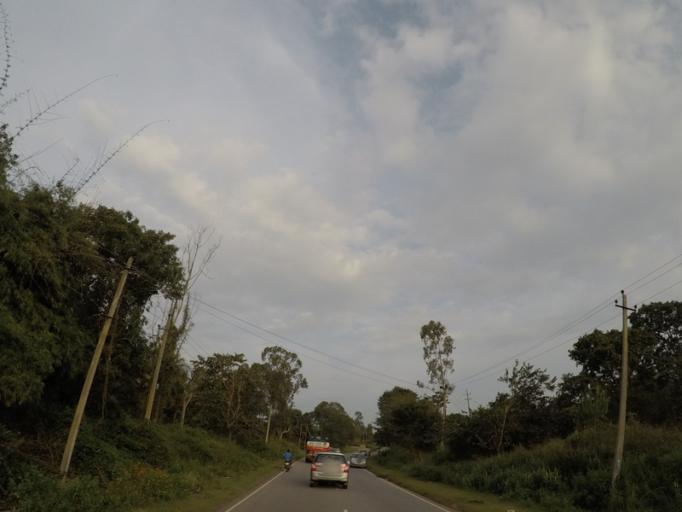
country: IN
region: Karnataka
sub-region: Hassan
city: Belur
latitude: 13.1355
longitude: 75.9590
